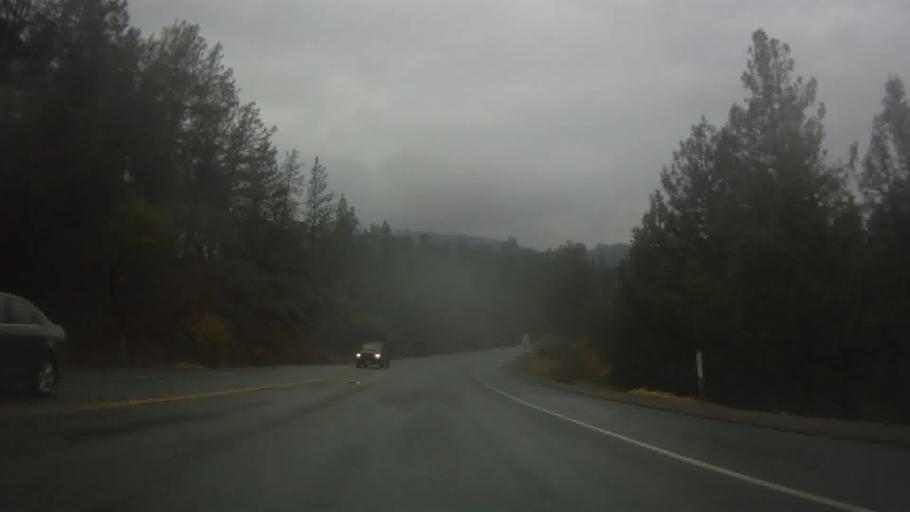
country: US
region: California
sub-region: Shasta County
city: Shasta
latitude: 40.5908
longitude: -122.4806
